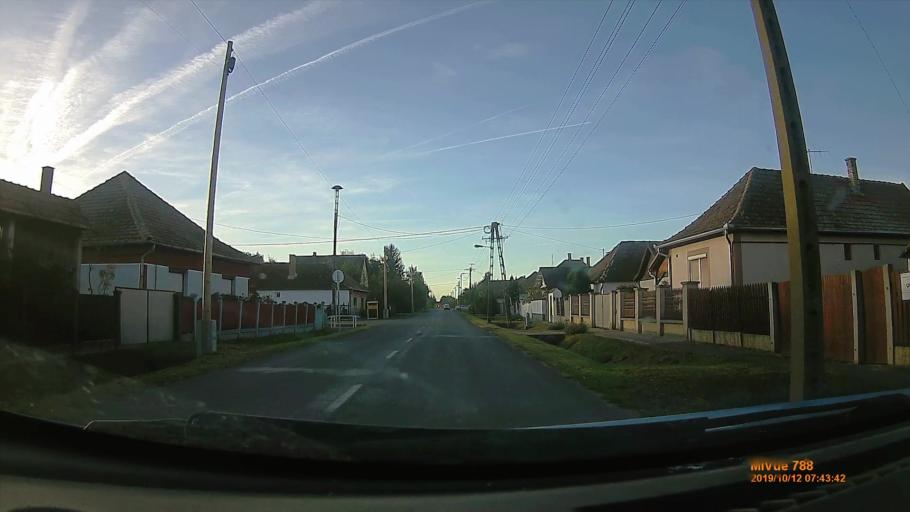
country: RO
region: Bihor
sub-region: Comuna Bors
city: Bors
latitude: 47.1916
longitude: 21.7876
